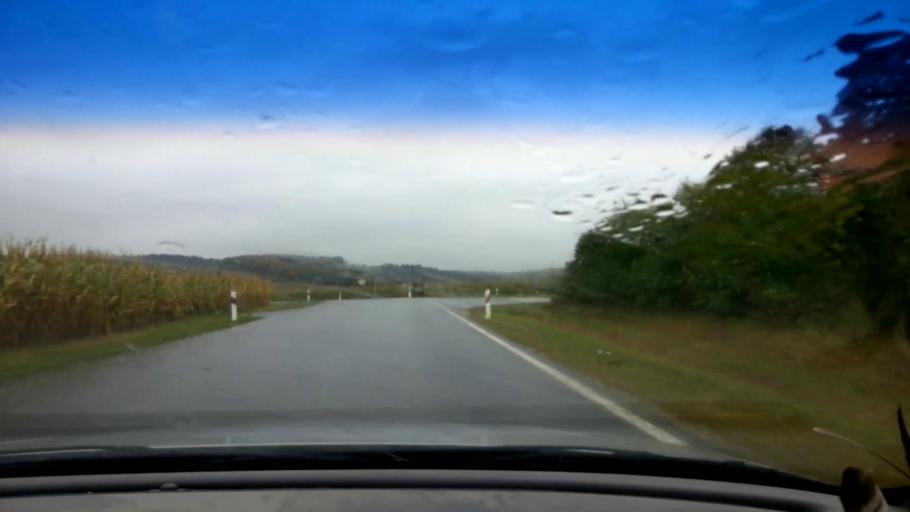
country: DE
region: Bavaria
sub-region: Upper Franconia
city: Poxdorf
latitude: 49.9093
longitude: 11.1446
